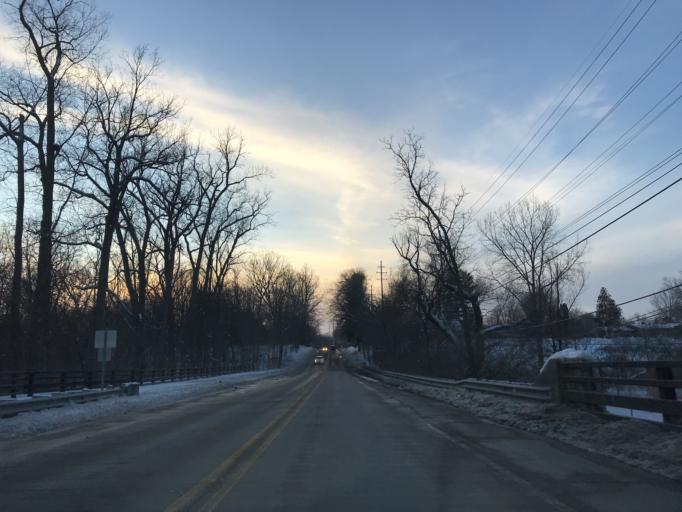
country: US
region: Michigan
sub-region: Oakland County
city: Franklin
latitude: 42.4569
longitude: -83.3057
